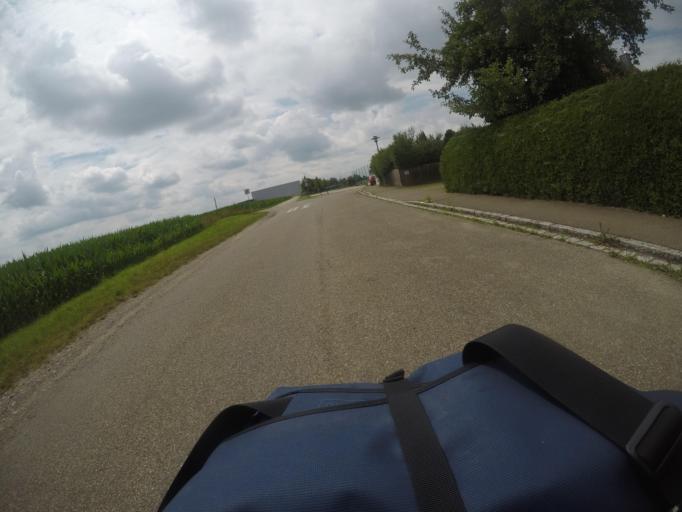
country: DE
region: Bavaria
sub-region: Swabia
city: Heimertingen
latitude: 48.0093
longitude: 10.1645
